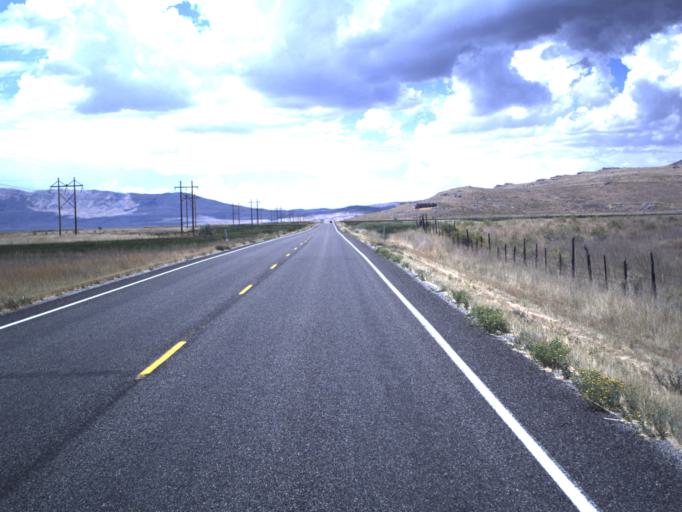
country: US
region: Utah
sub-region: Box Elder County
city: Tremonton
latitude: 41.6110
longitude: -112.3502
